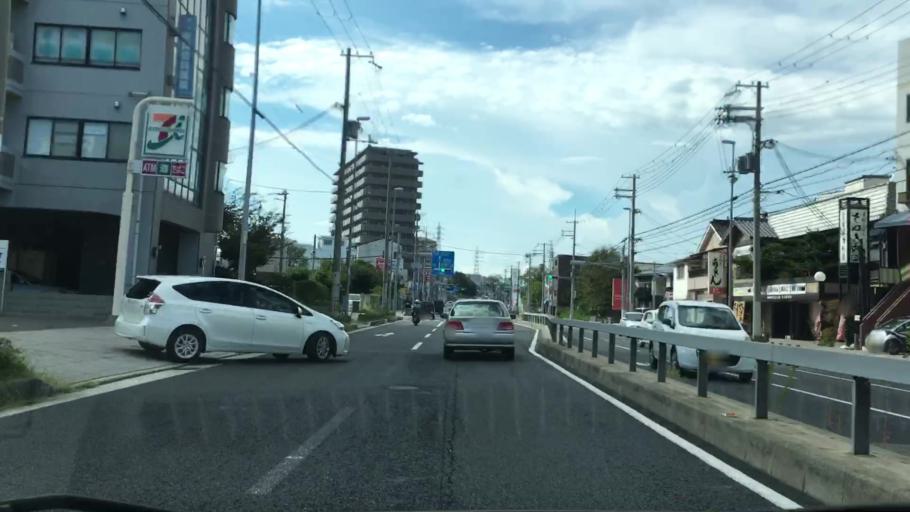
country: JP
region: Hyogo
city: Akashi
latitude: 34.6519
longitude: 134.9785
